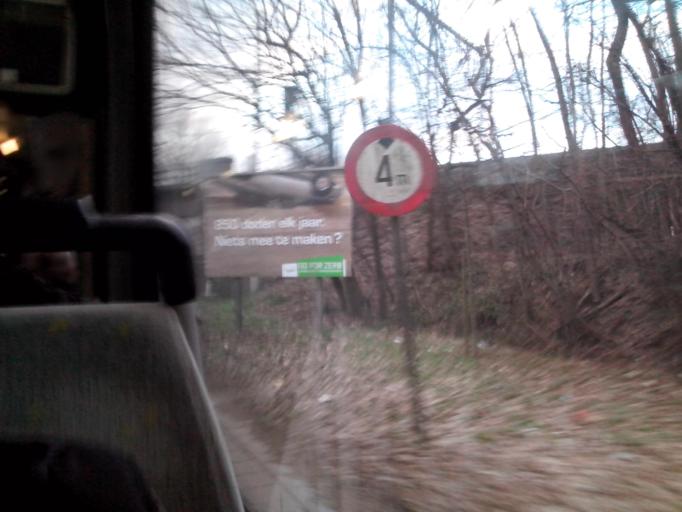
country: BE
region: Flanders
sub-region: Provincie Vlaams-Brabant
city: Dilbeek
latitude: 50.8918
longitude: 4.2530
